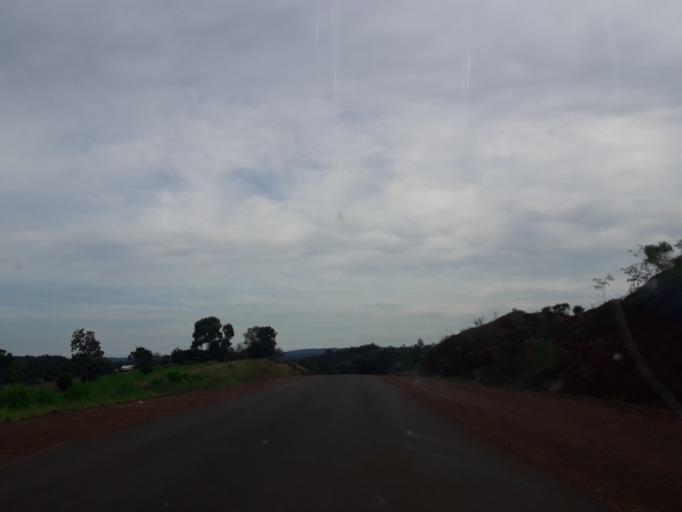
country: AR
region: Misiones
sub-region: Departamento de San Pedro
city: San Pedro
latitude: -26.5216
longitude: -53.9394
